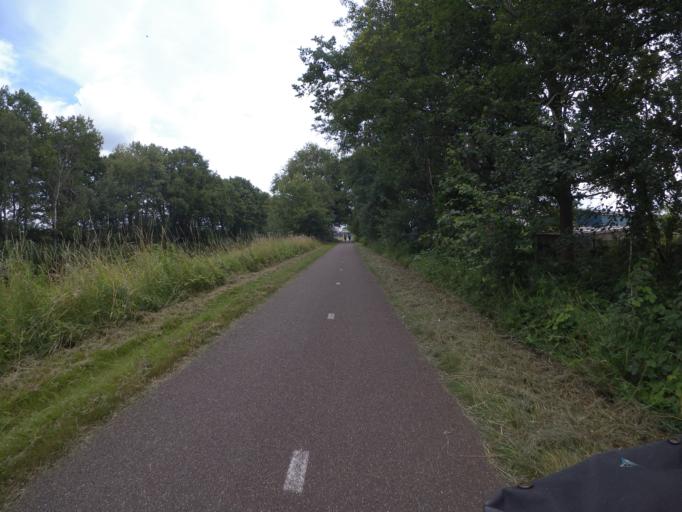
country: NL
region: North Brabant
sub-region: Gemeente Son en Breugel
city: Son
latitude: 51.5043
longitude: 5.4679
